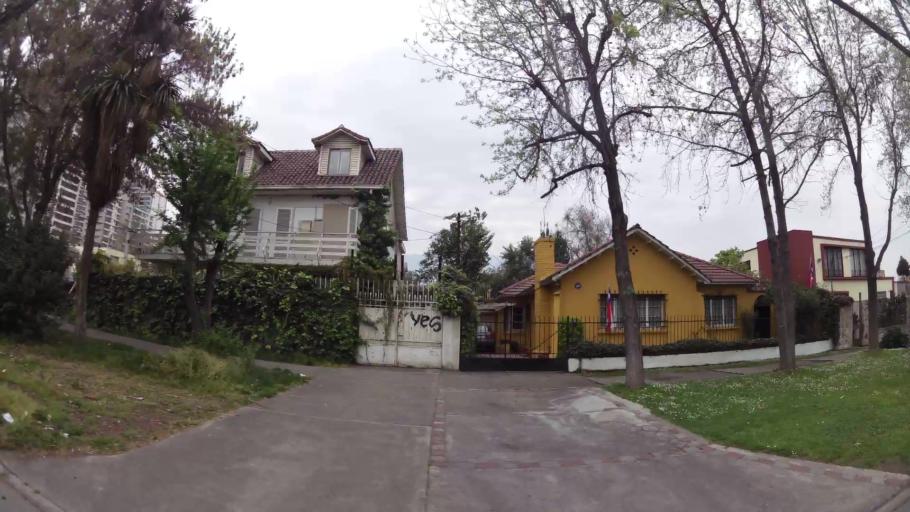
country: CL
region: Santiago Metropolitan
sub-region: Provincia de Santiago
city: Villa Presidente Frei, Nunoa, Santiago, Chile
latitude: -33.4566
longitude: -70.5861
